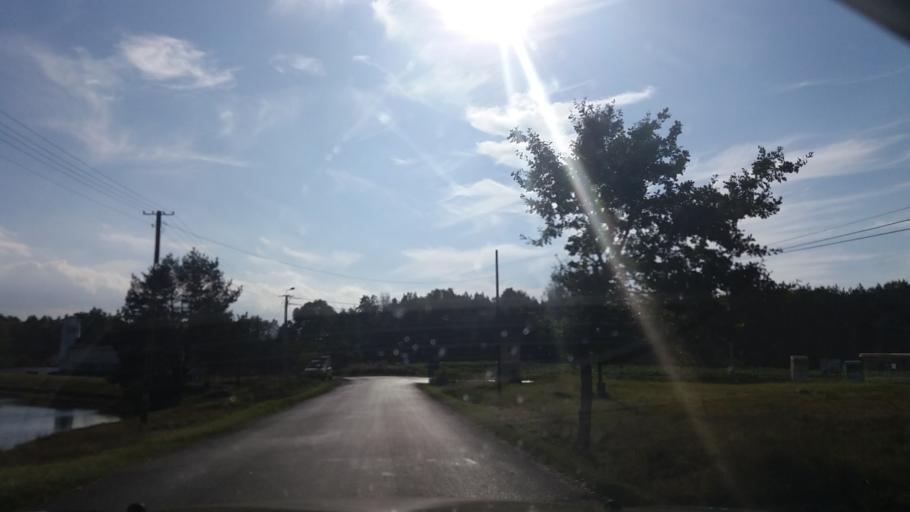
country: PL
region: Lesser Poland Voivodeship
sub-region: Powiat chrzanowski
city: Alwernia
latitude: 50.0425
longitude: 19.5454
